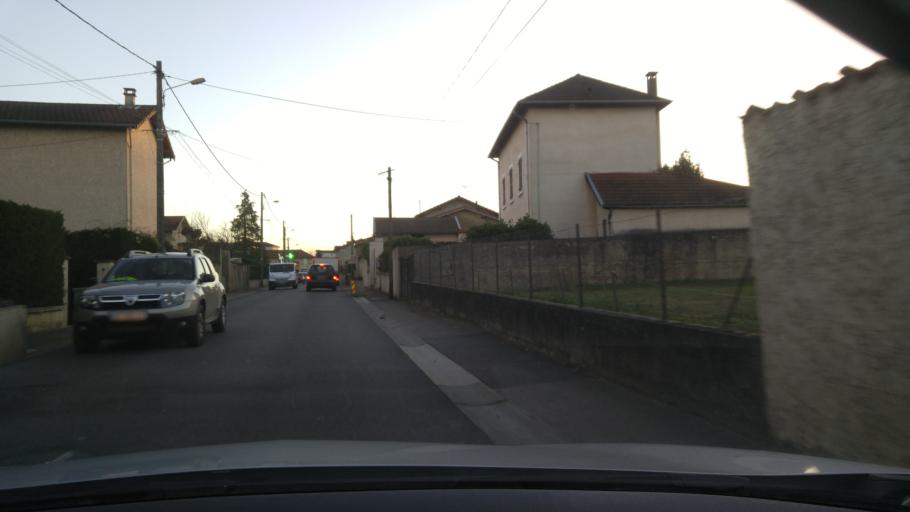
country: FR
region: Rhone-Alpes
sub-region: Departement de l'Isere
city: Tignieu-Jameyzieu
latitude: 45.7386
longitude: 5.1875
